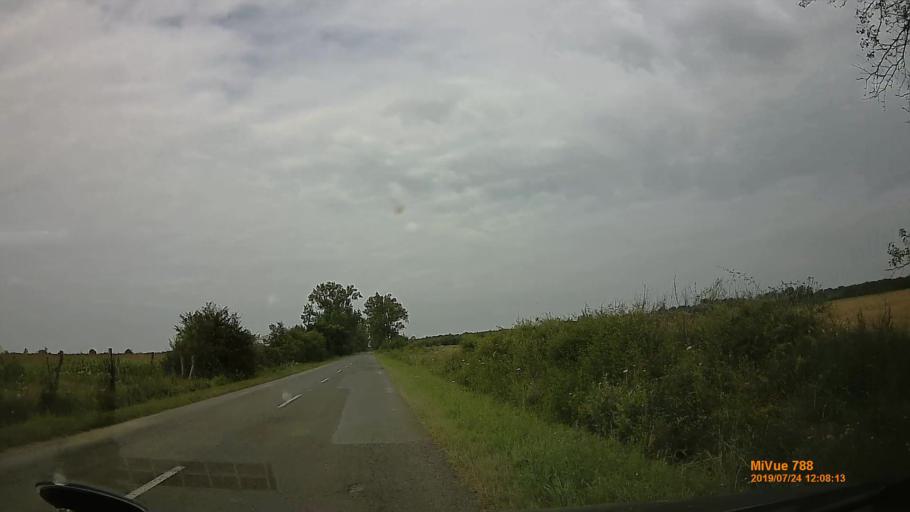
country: HU
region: Szabolcs-Szatmar-Bereg
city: Vasarosnameny
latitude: 48.1943
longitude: 22.3863
